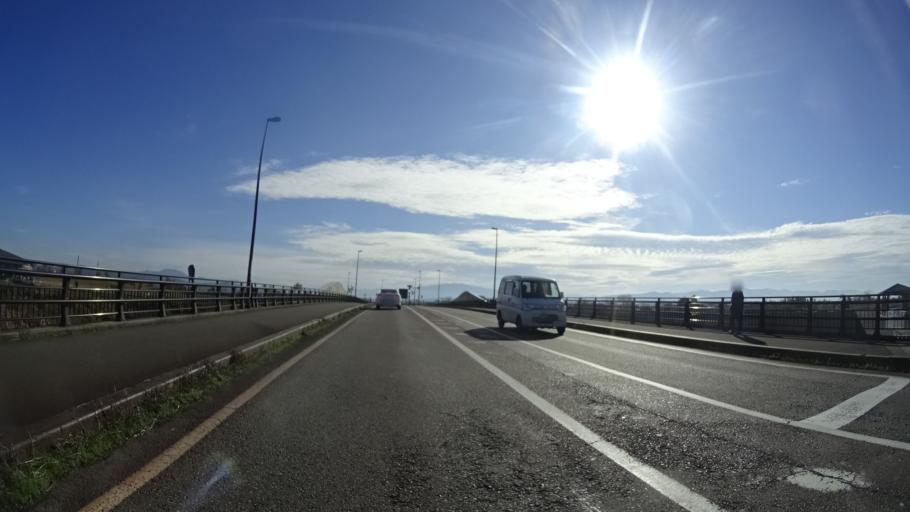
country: JP
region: Niigata
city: Mitsuke
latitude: 37.5457
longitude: 138.8817
